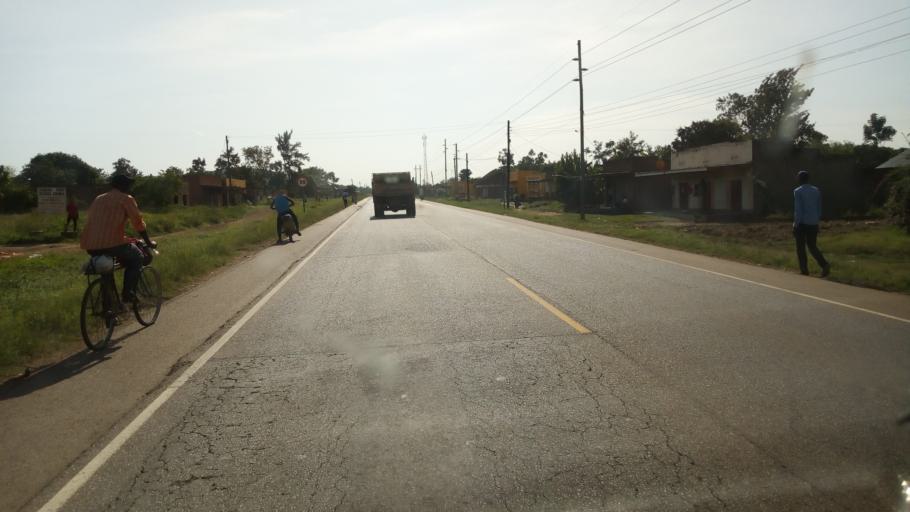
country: UG
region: Eastern Region
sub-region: Bugiri District
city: Bugiri
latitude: 0.5312
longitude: 33.8699
